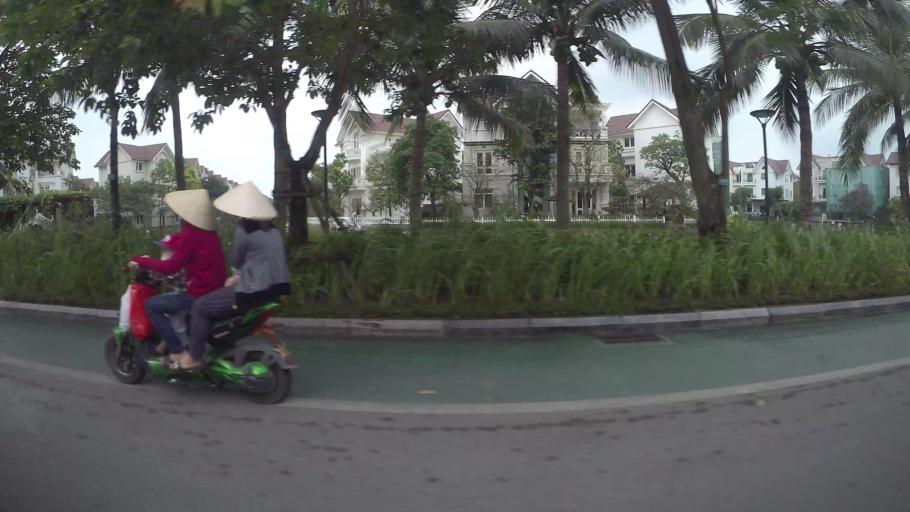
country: VN
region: Ha Noi
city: Trau Quy
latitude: 21.0459
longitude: 105.9170
